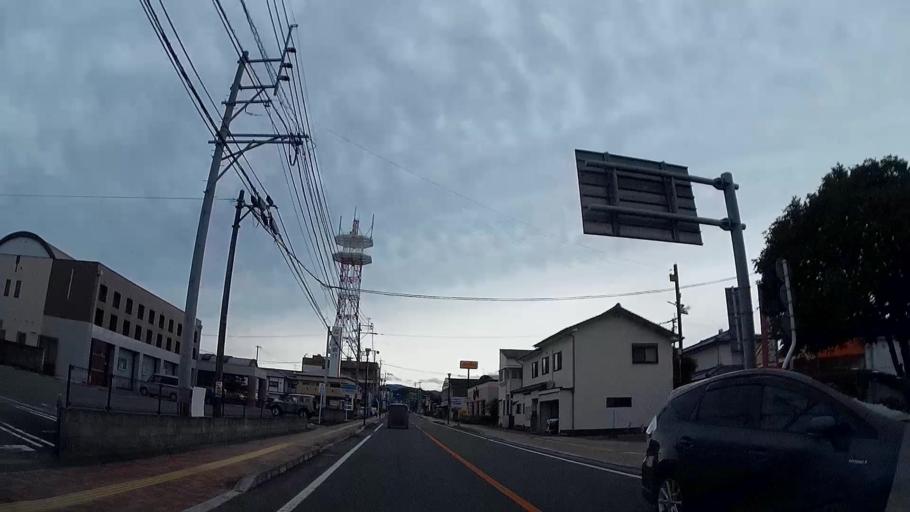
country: JP
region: Kumamoto
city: Kikuchi
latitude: 32.9789
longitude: 130.8071
